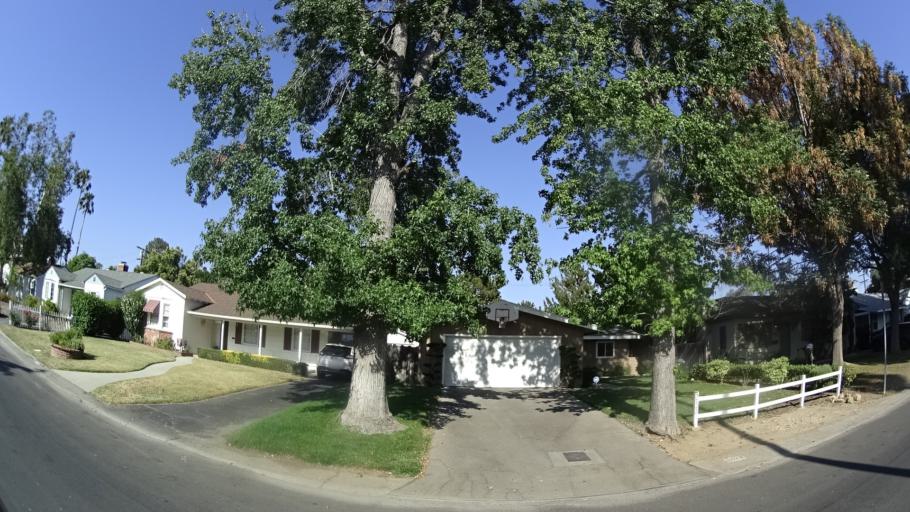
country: US
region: California
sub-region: Los Angeles County
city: Van Nuys
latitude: 34.1746
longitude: -118.4510
